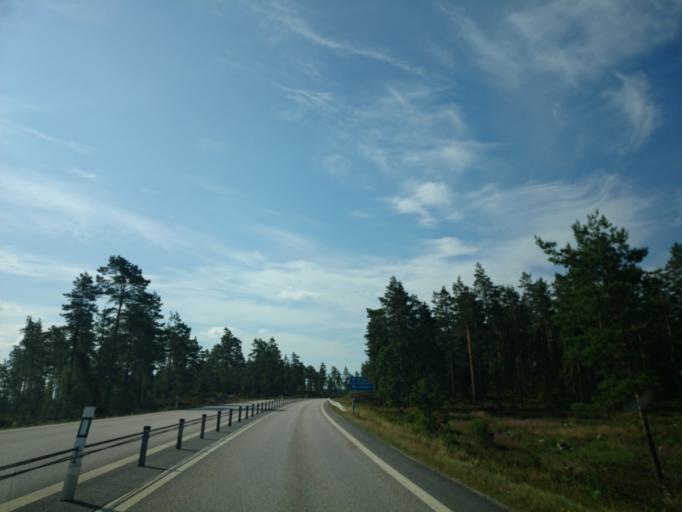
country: SE
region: Kalmar
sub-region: Vasterviks Kommun
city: Forserum
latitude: 58.0625
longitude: 16.5276
